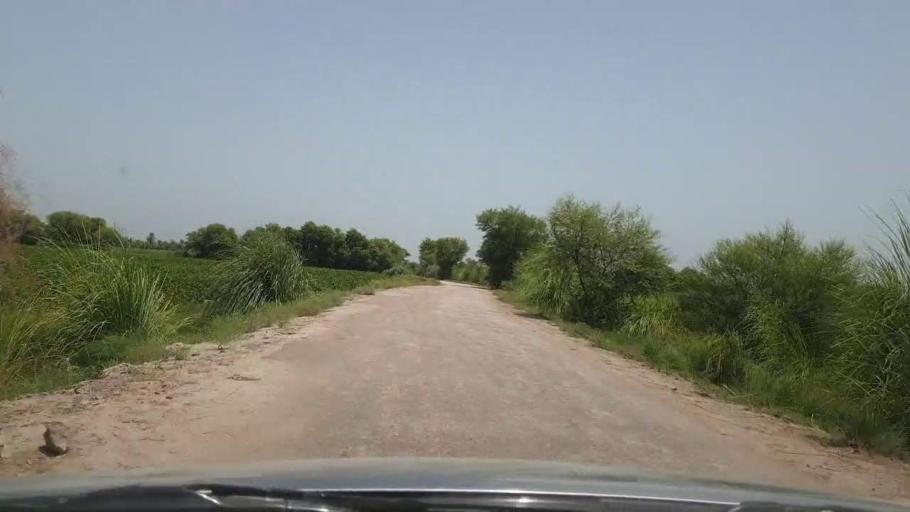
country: PK
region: Sindh
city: Pano Aqil
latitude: 27.8688
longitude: 69.1729
